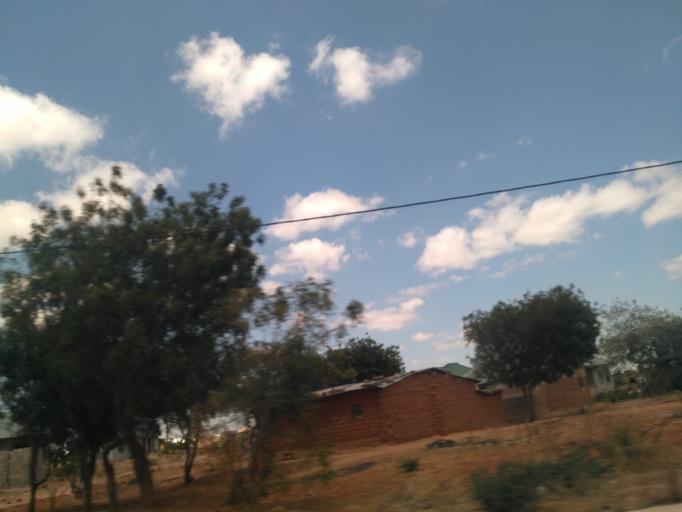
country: TZ
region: Dodoma
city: Kisasa
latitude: -6.1808
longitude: 35.7864
